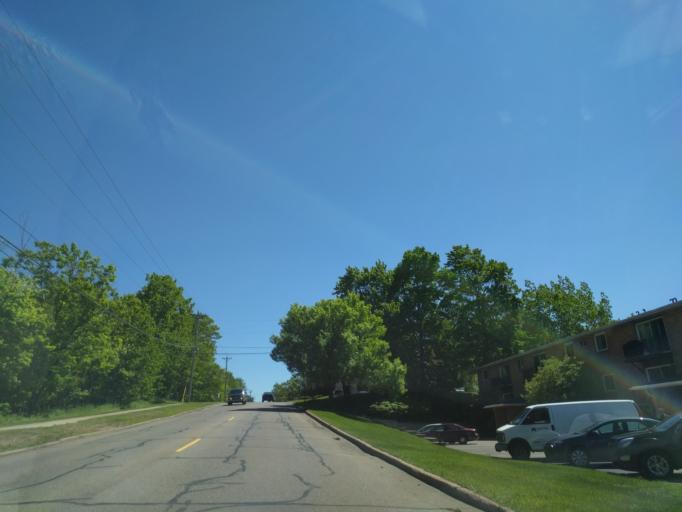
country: US
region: Michigan
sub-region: Marquette County
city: Marquette
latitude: 46.5526
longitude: -87.4123
